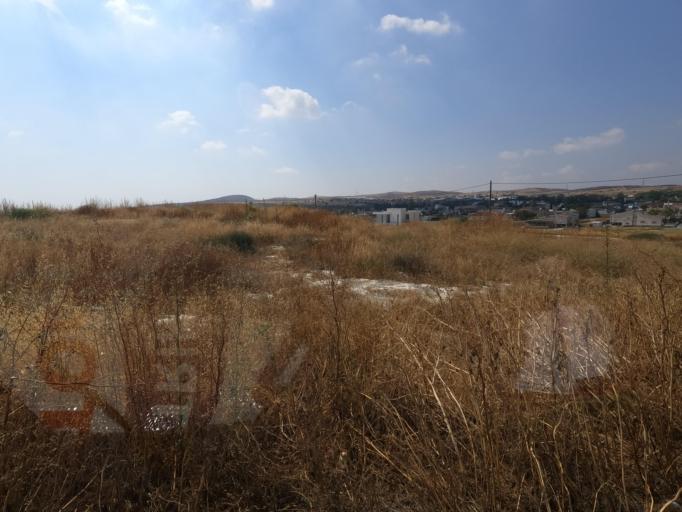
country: CY
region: Lefkosia
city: Lympia
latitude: 34.9978
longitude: 33.4678
